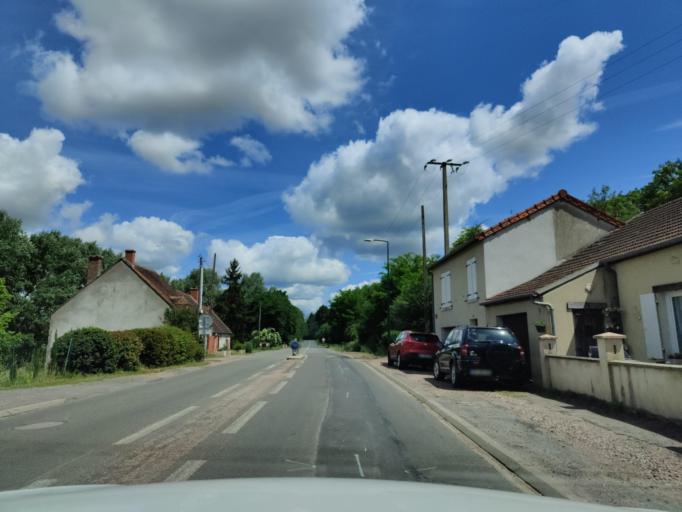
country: FR
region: Auvergne
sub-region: Departement de l'Allier
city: Vallon-en-Sully
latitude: 46.6286
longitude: 2.5914
